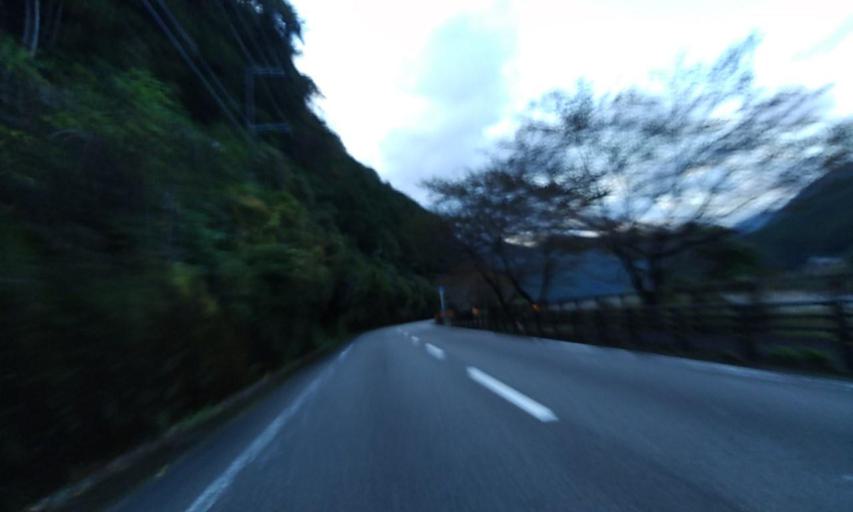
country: JP
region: Wakayama
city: Shingu
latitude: 33.7271
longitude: 135.9523
